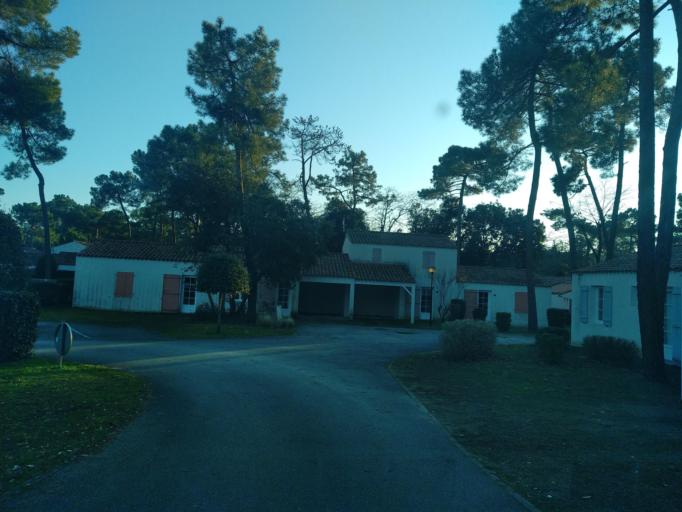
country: FR
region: Pays de la Loire
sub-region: Departement de la Vendee
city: Longeville-sur-Mer
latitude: 46.3899
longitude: -1.4830
